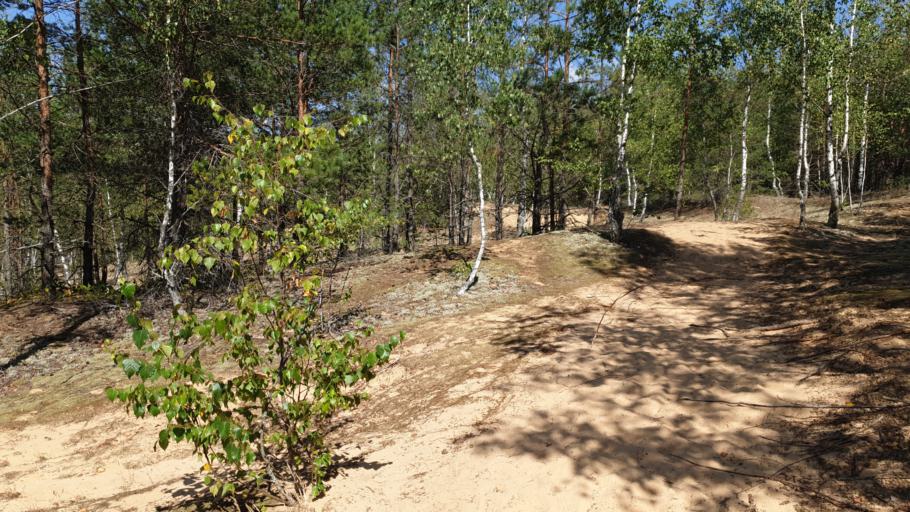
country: LT
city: Sirvintos
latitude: 54.8920
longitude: 24.9534
